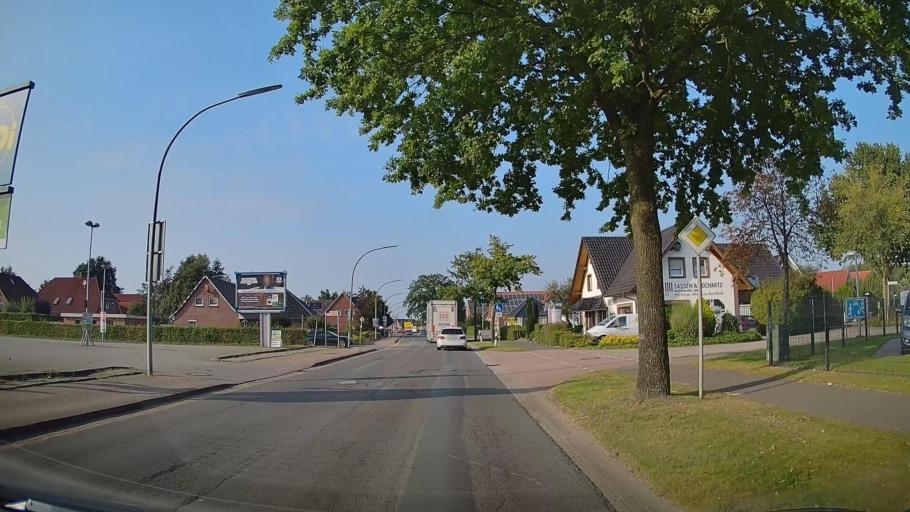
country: DE
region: Lower Saxony
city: Friesoythe
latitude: 53.0293
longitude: 7.8563
